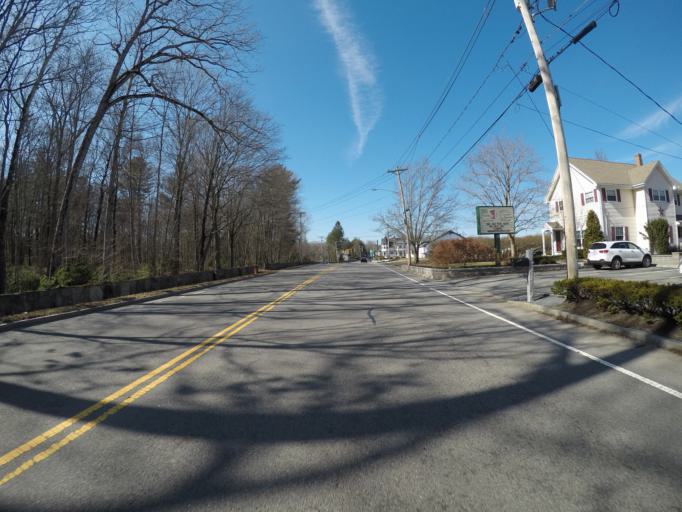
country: US
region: Massachusetts
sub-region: Norfolk County
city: Stoughton
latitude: 42.0671
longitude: -71.0856
